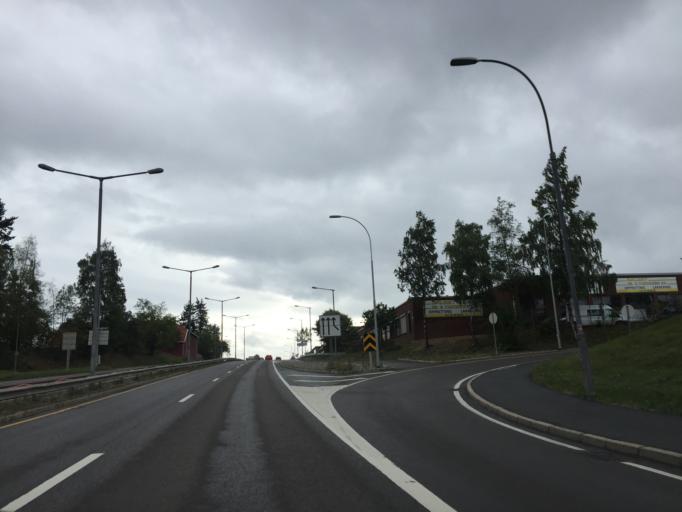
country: NO
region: Oslo
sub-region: Oslo
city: Oslo
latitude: 59.9330
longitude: 10.8284
